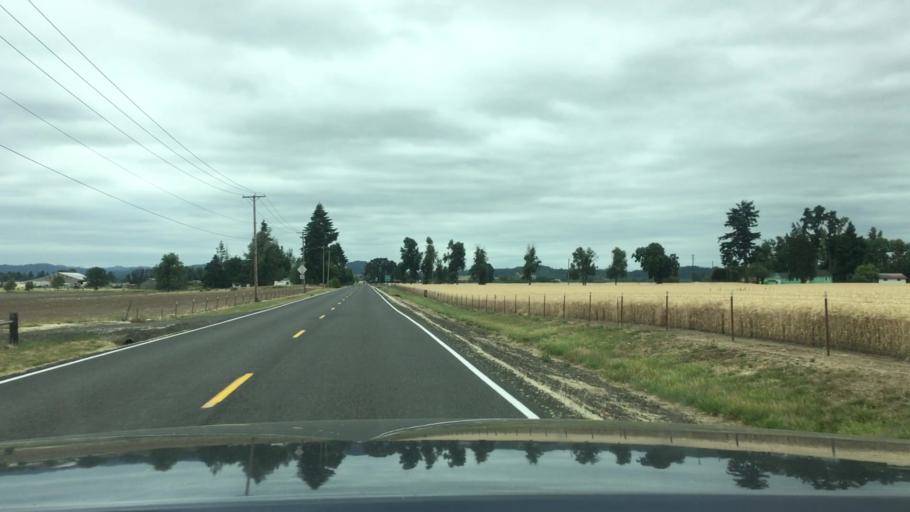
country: US
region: Oregon
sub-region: Lane County
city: Junction City
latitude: 44.1095
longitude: -123.2084
